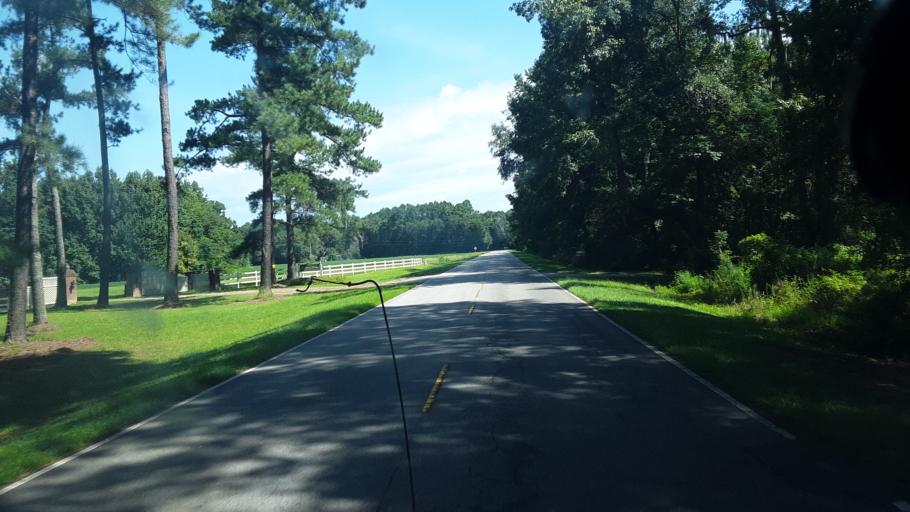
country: US
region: South Carolina
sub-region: Hampton County
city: Hampton
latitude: 33.0119
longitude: -81.0441
